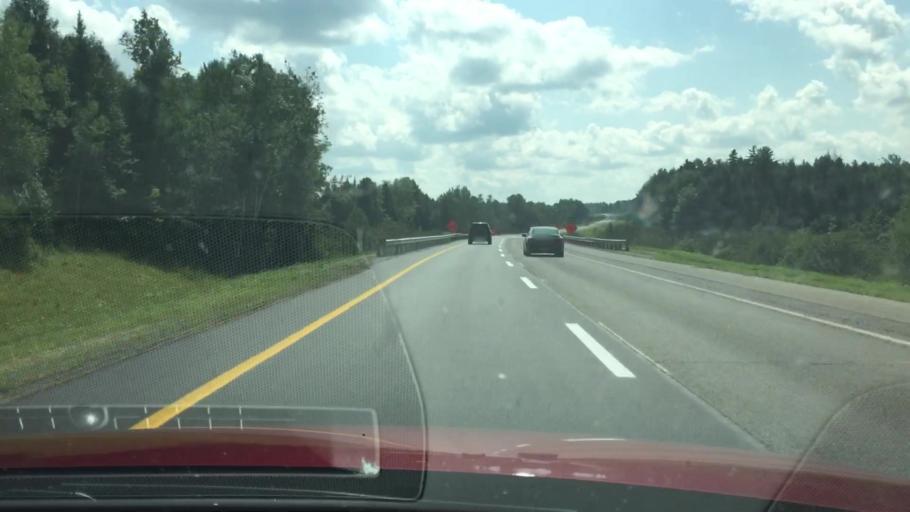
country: US
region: Maine
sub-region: Penobscot County
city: Medway
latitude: 45.6406
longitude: -68.5000
